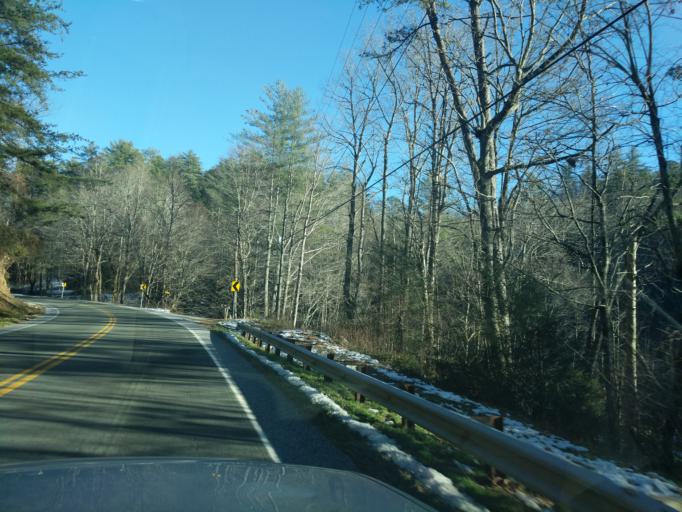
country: US
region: Georgia
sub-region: Rabun County
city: Clayton
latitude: 34.8705
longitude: -83.4655
